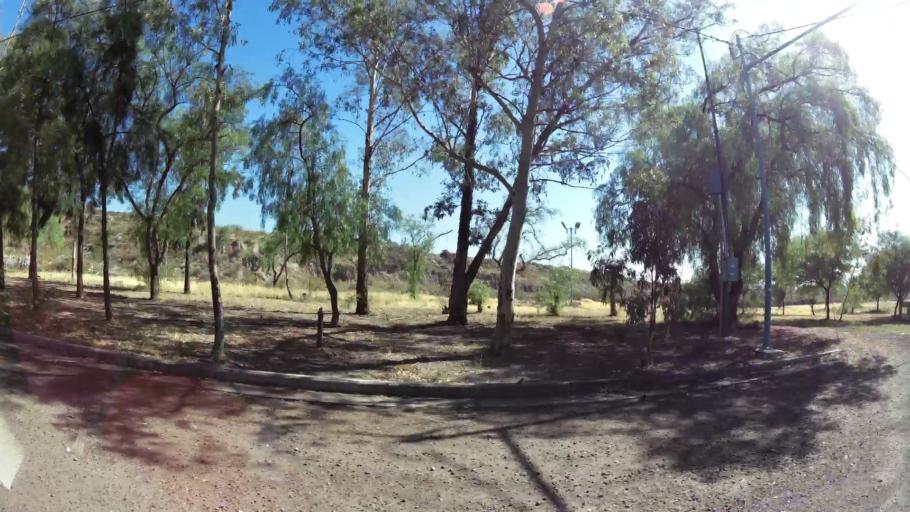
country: AR
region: Mendoza
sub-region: Departamento de Godoy Cruz
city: Godoy Cruz
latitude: -32.9002
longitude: -68.8888
